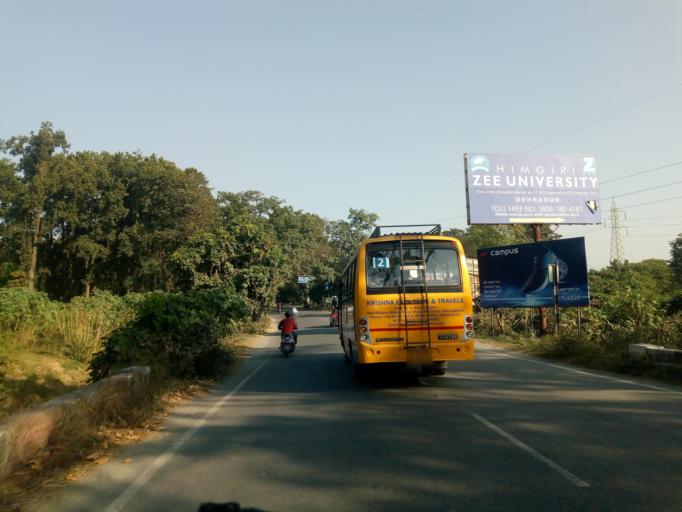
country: IN
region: Uttarakhand
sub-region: Dehradun
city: Vikasnagar
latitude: 30.3475
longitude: 77.8711
